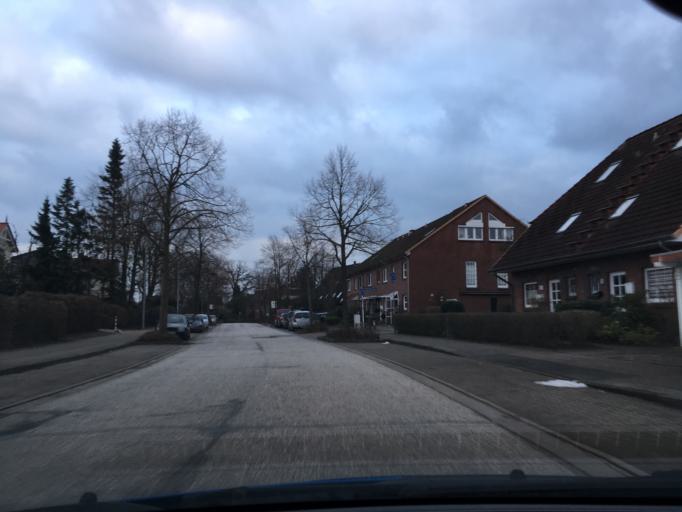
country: DE
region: Schleswig-Holstein
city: Wedel
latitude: 53.5885
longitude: 9.6956
